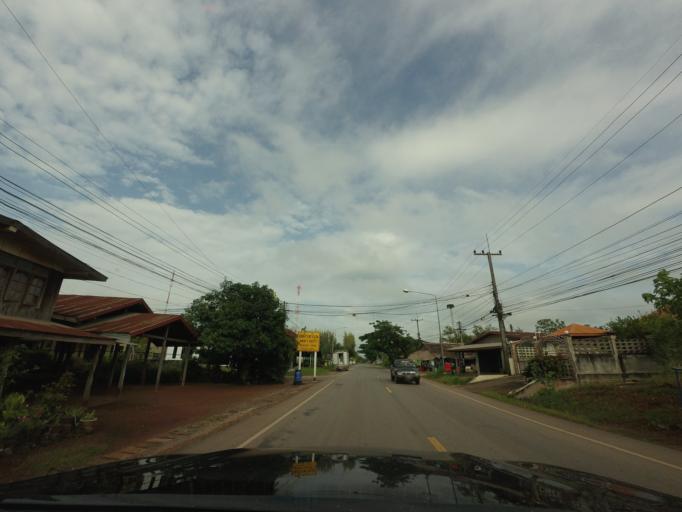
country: TH
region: Changwat Udon Thani
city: Nam Som
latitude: 17.8024
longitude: 102.2785
